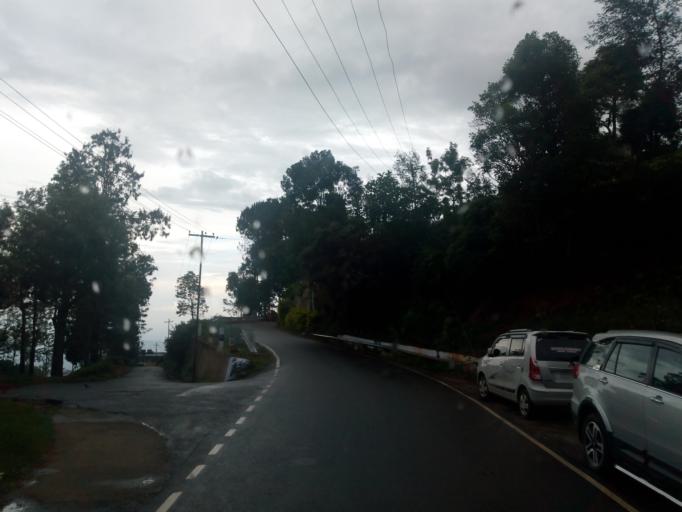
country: IN
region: Tamil Nadu
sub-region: Nilgiri
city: Wellington
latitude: 11.3533
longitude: 76.8317
